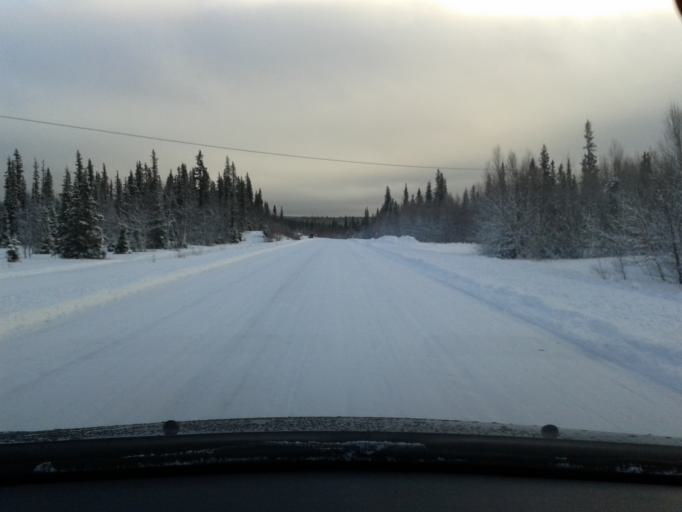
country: SE
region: Vaesterbotten
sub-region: Vilhelmina Kommun
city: Sjoberg
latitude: 65.2573
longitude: 15.6983
